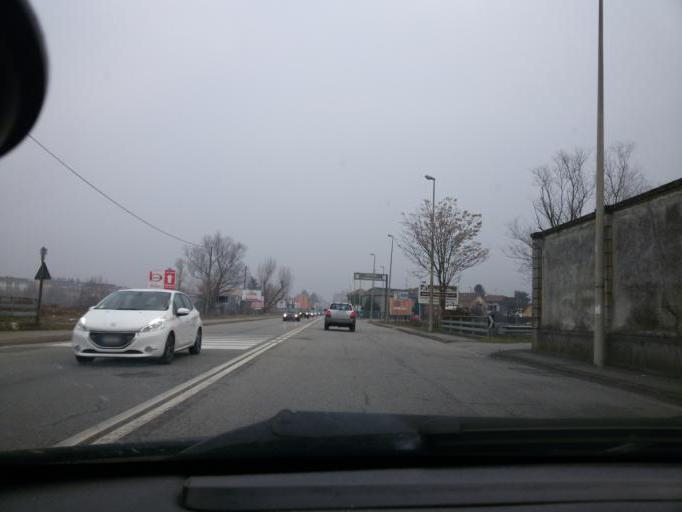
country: IT
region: Piedmont
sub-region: Provincia di Vercelli
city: Vercelli
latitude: 45.3121
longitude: 8.4054
